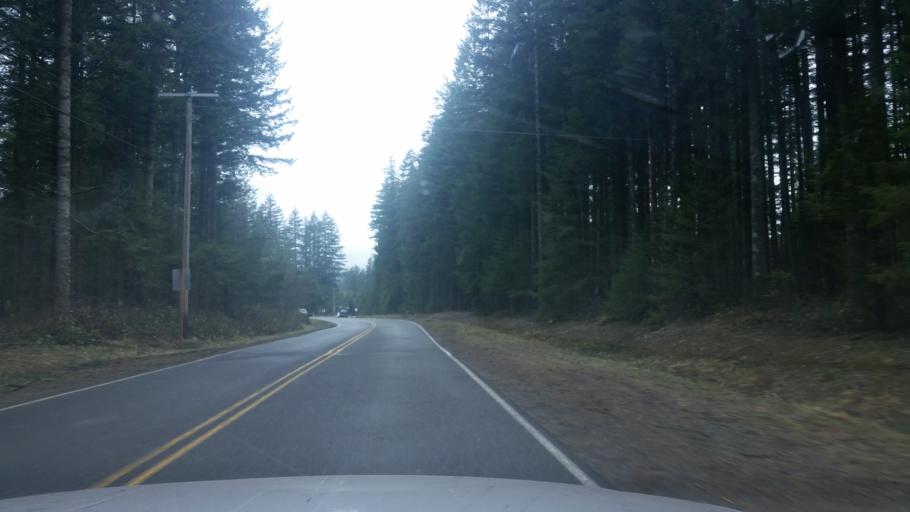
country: US
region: Washington
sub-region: King County
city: Tanner
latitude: 47.4727
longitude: -121.7271
